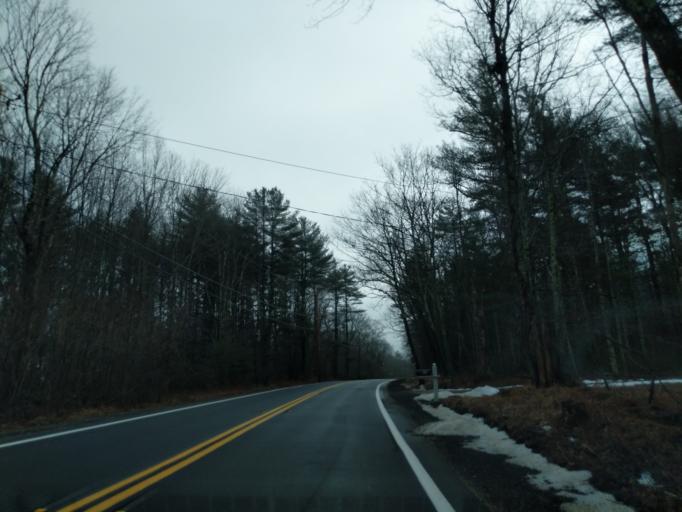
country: US
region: Massachusetts
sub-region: Worcester County
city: Douglas
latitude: 42.0554
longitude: -71.7604
